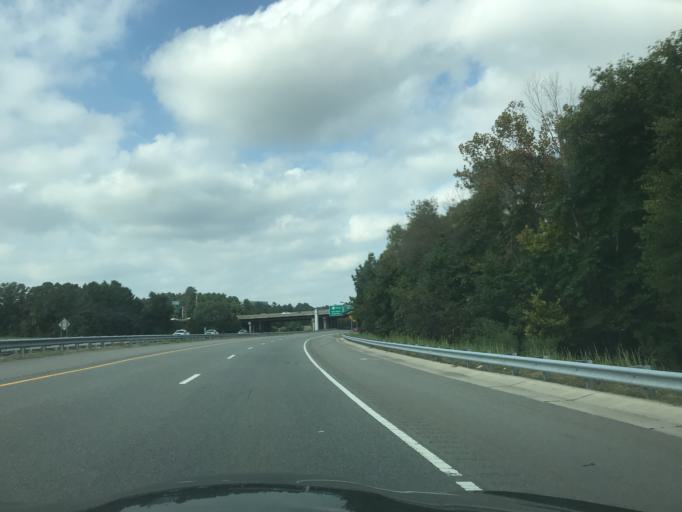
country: US
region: North Carolina
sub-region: Wake County
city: Morrisville
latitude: 35.8984
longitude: -78.8760
